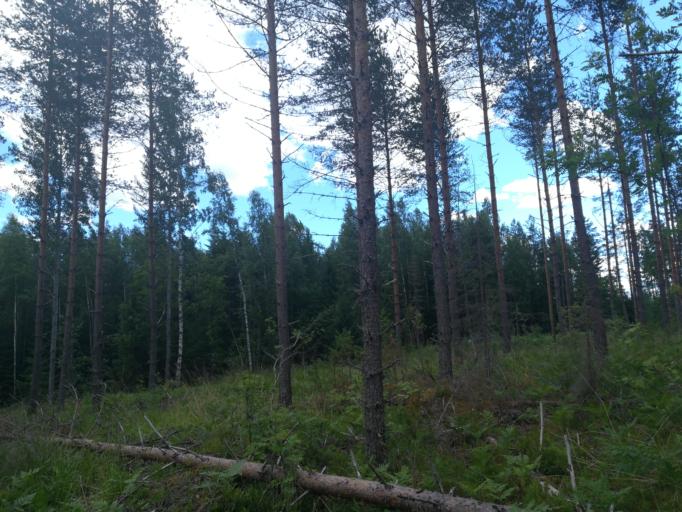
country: FI
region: Southern Savonia
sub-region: Mikkeli
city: Hirvensalmi
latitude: 61.7058
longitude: 26.9722
